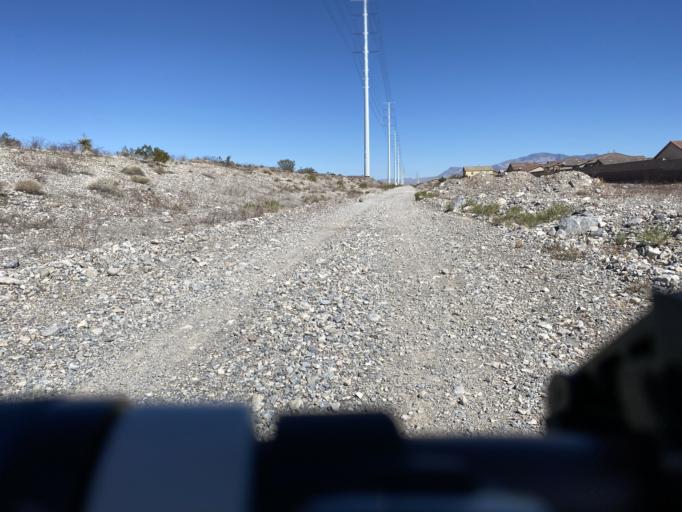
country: US
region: Nevada
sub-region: Clark County
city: Summerlin South
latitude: 36.2935
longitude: -115.3335
